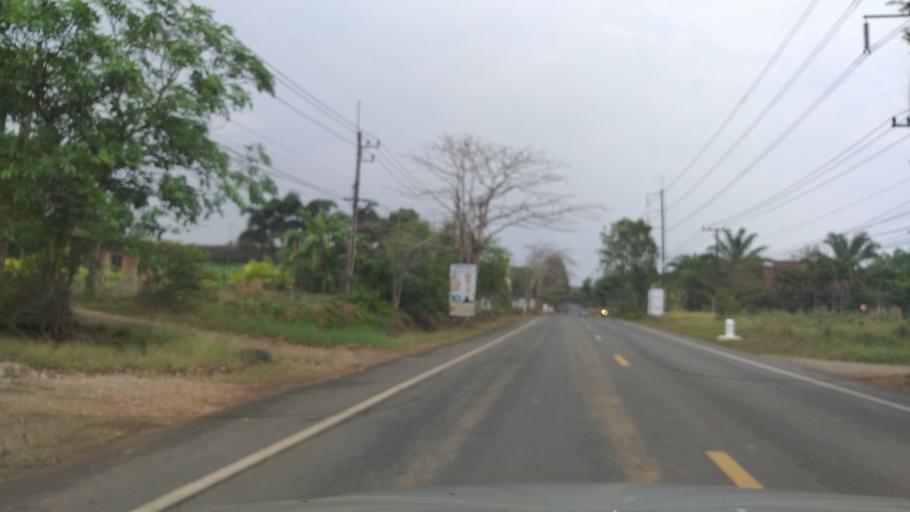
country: TH
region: Trat
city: Khao Saming
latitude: 12.3218
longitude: 102.3630
